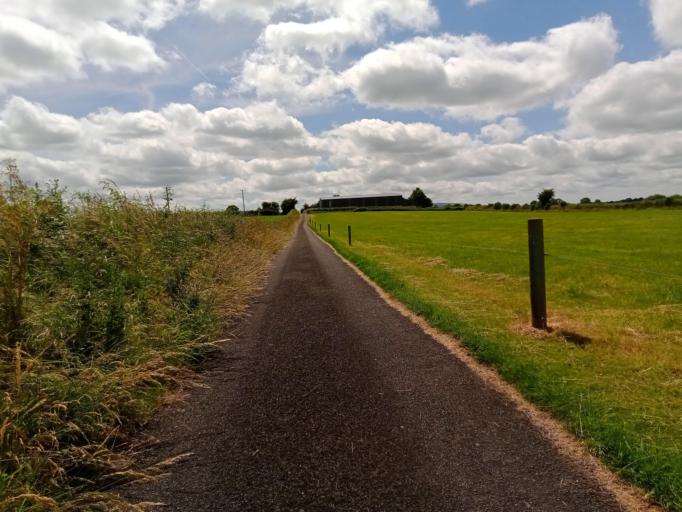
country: IE
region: Leinster
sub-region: Kilkenny
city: Callan
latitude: 52.5492
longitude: -7.4177
